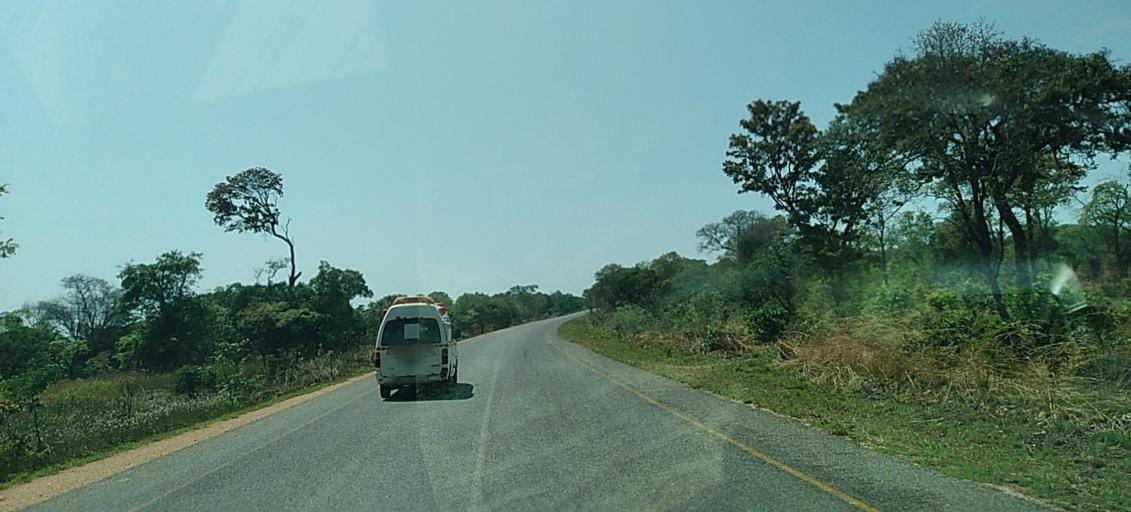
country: ZM
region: North-Western
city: Solwezi
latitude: -12.2866
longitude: 25.7873
